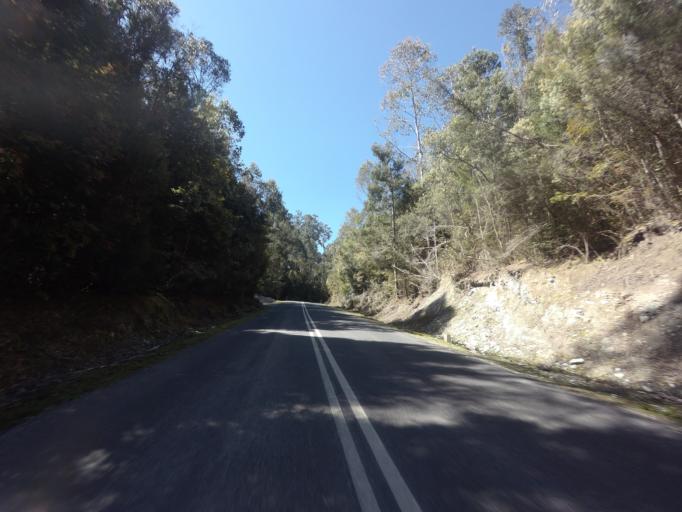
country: AU
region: Tasmania
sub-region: Derwent Valley
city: New Norfolk
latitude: -42.7247
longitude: 146.4346
